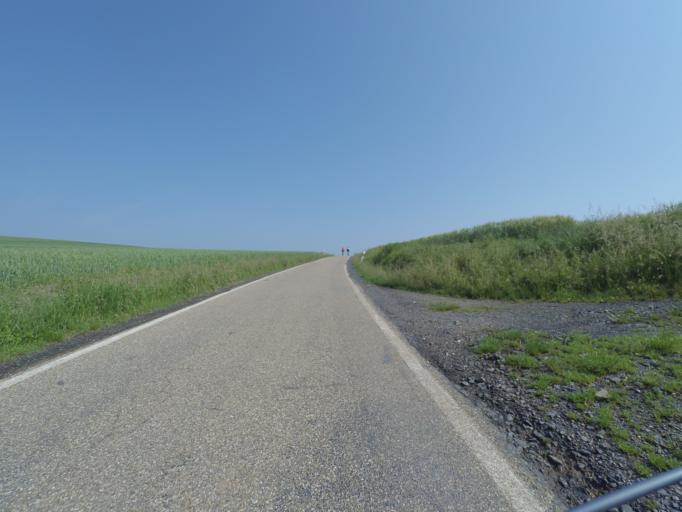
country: DE
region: Rheinland-Pfalz
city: Montenich
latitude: 50.2159
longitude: 7.3030
